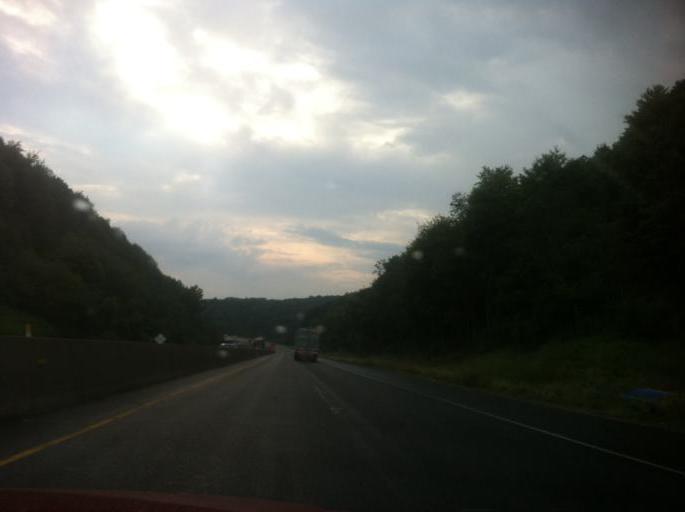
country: US
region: Pennsylvania
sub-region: Clarion County
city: Marianne
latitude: 41.1967
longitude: -79.4622
